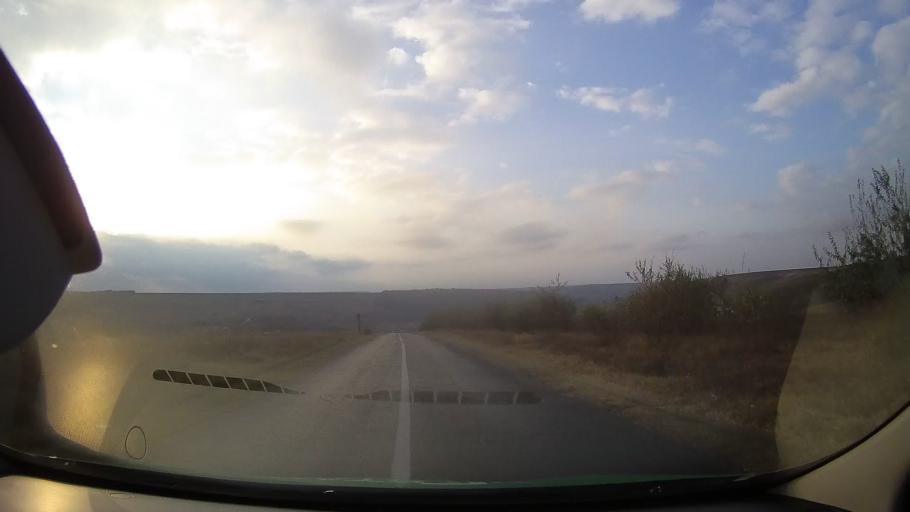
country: RO
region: Constanta
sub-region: Comuna Adamclisi
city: Adamclisi
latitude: 44.0208
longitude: 27.8843
